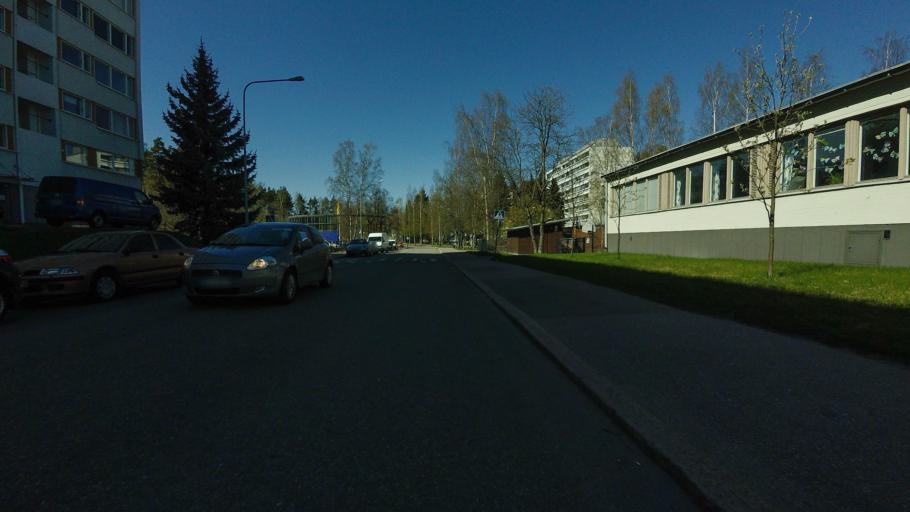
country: FI
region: Uusimaa
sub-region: Helsinki
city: Vantaa
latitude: 60.2121
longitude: 25.0778
